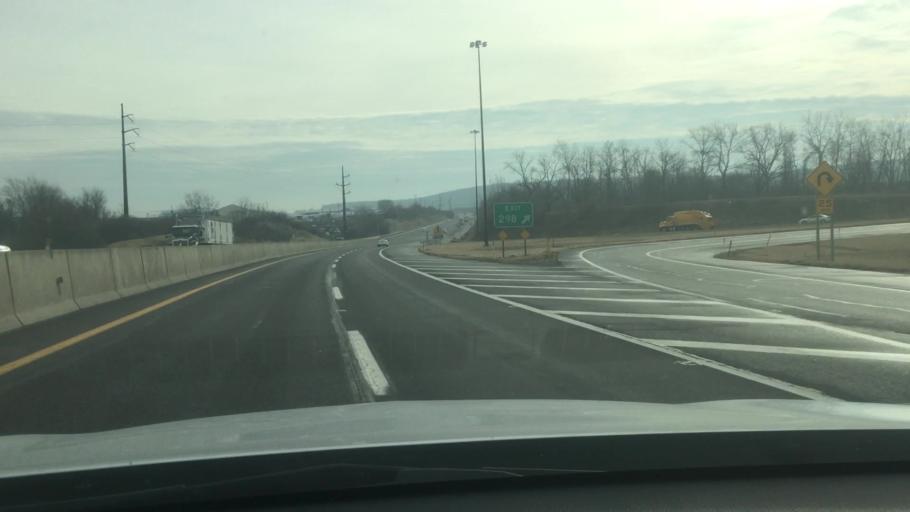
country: US
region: Pennsylvania
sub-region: Chester County
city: Elverson
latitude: 40.1595
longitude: -75.8814
